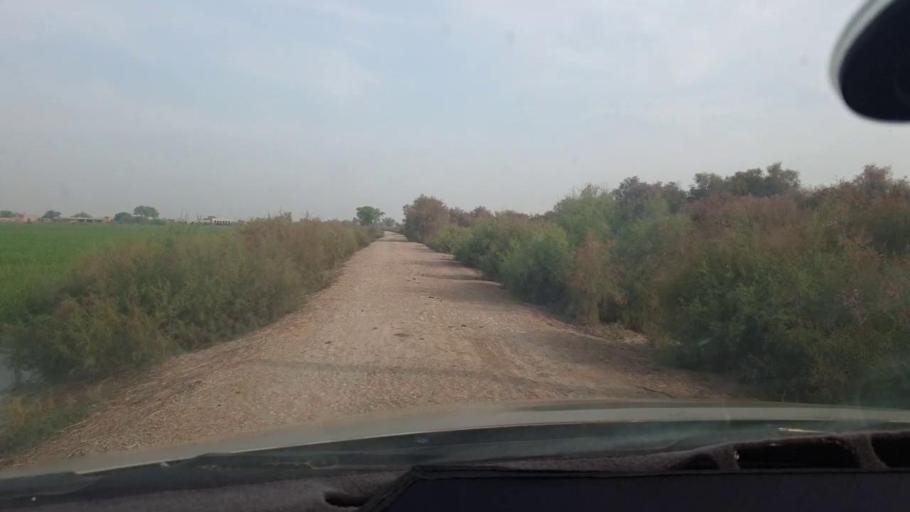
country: PK
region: Balochistan
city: Jhatpat
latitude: 28.3670
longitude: 68.4049
